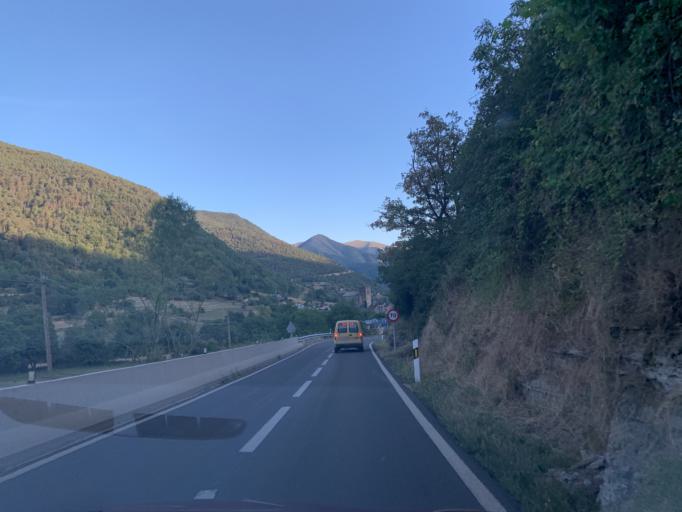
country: ES
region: Aragon
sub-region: Provincia de Huesca
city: Broto
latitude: 42.6088
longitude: -0.1232
